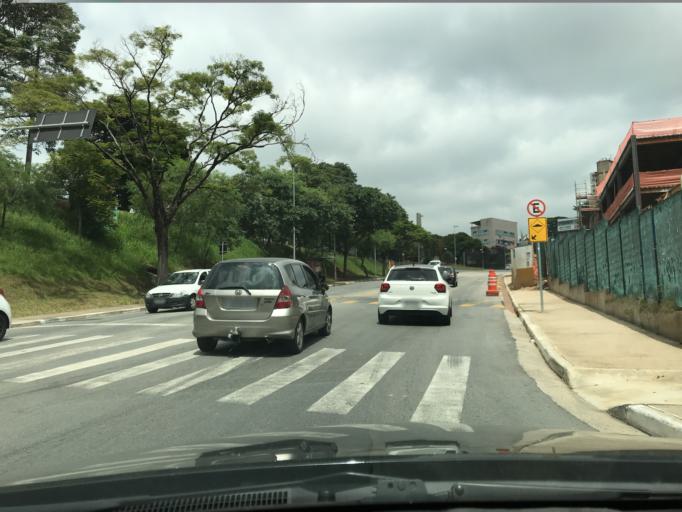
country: BR
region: Sao Paulo
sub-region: Barueri
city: Barueri
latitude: -23.5041
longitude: -46.8703
